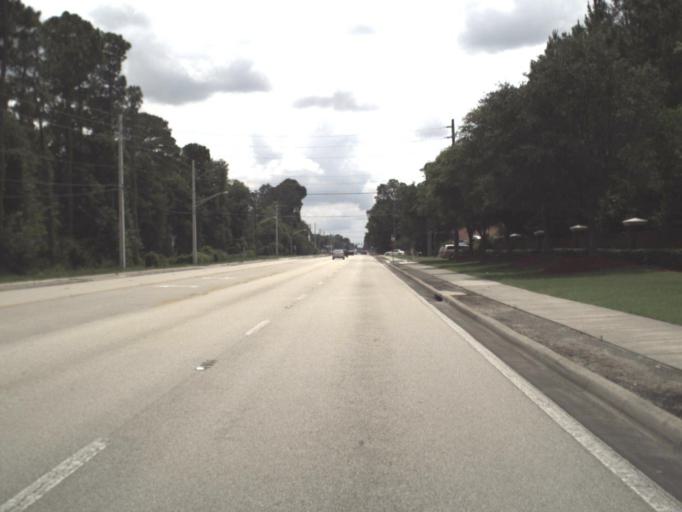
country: US
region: Florida
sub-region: Duval County
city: Jacksonville
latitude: 30.4385
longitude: -81.7057
